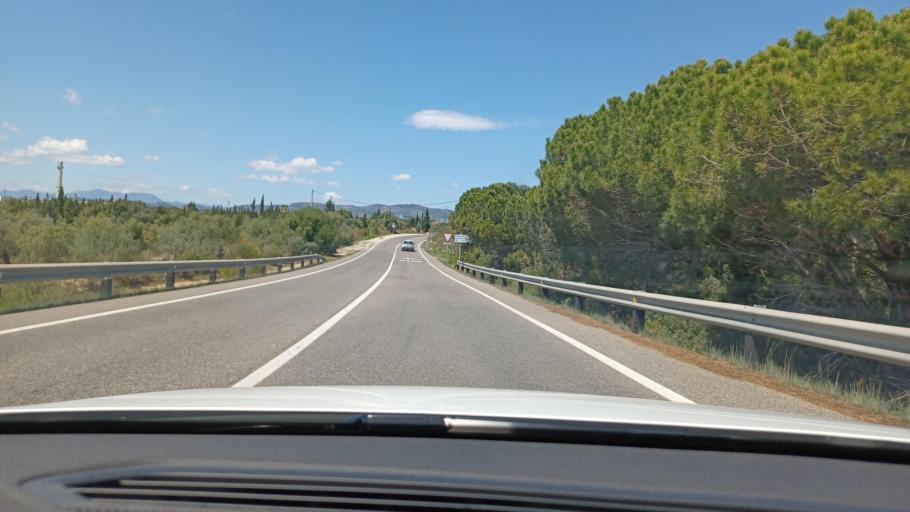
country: ES
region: Catalonia
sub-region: Provincia de Tarragona
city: L'Ampolla
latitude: 40.8020
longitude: 0.6914
